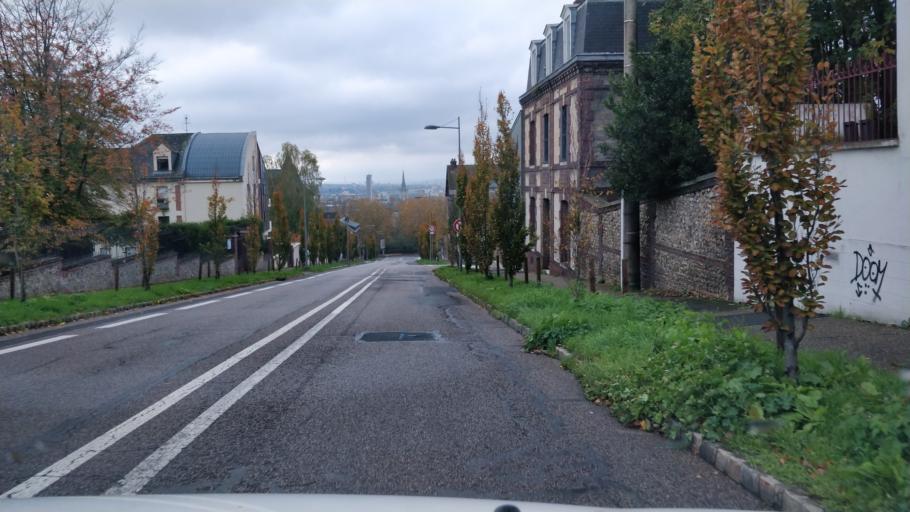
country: FR
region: Haute-Normandie
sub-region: Departement de la Seine-Maritime
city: Rouen
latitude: 49.4474
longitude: 1.1108
